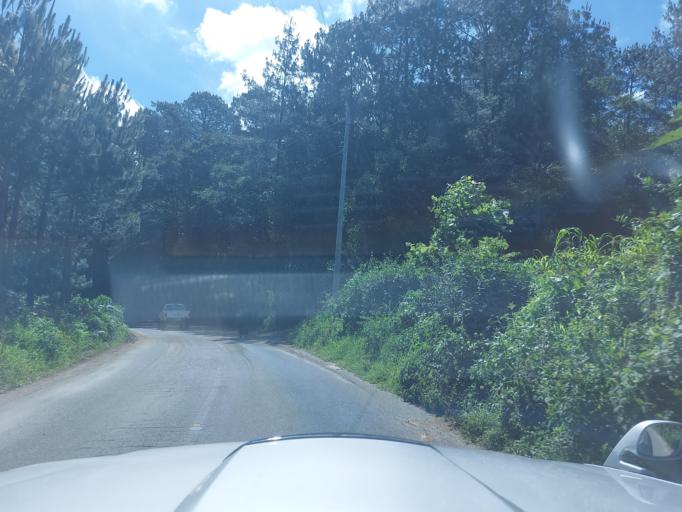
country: GT
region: Chimaltenango
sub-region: Municipio de San Juan Comalapa
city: Comalapa
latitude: 14.7121
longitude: -90.8903
